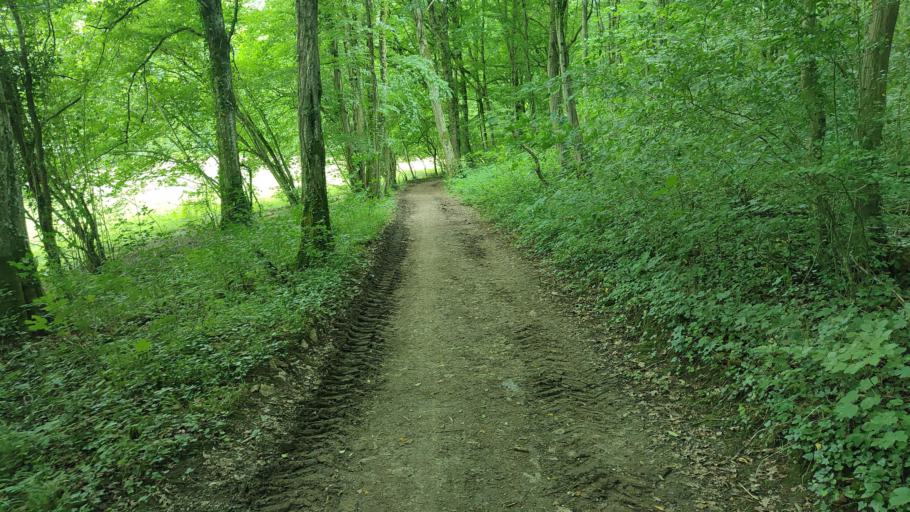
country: BE
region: Wallonia
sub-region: Province du Hainaut
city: Chimay
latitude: 50.0630
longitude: 4.3858
